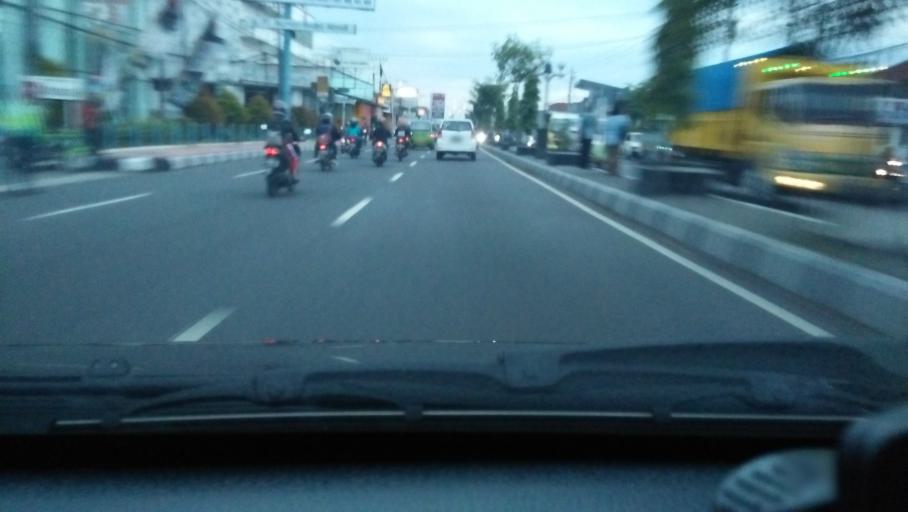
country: ID
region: Central Java
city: Mertoyudan
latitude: -7.5066
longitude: 110.2243
